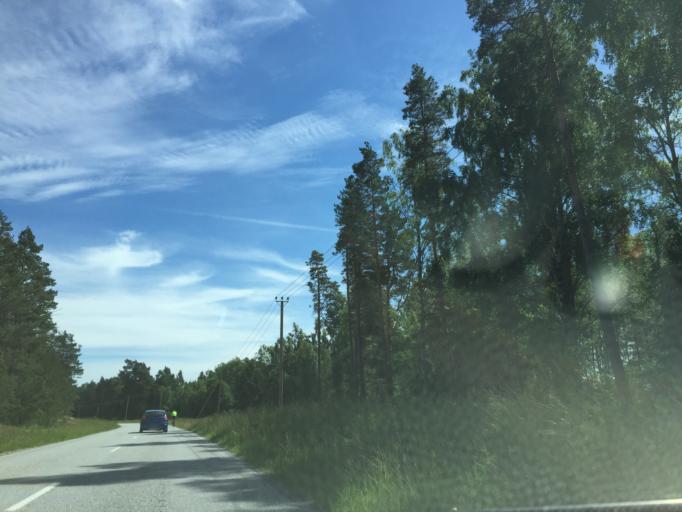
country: LV
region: Talsu Rajons
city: Valdemarpils
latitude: 57.5912
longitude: 22.6092
